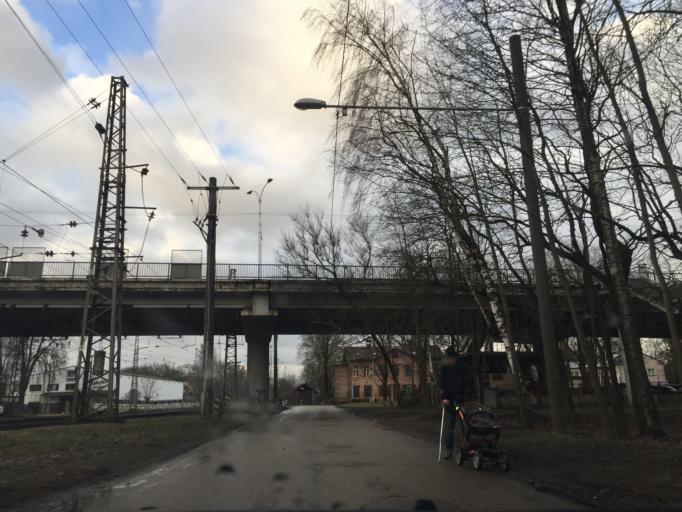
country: LV
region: Marupe
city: Marupe
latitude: 56.9399
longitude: 24.0527
